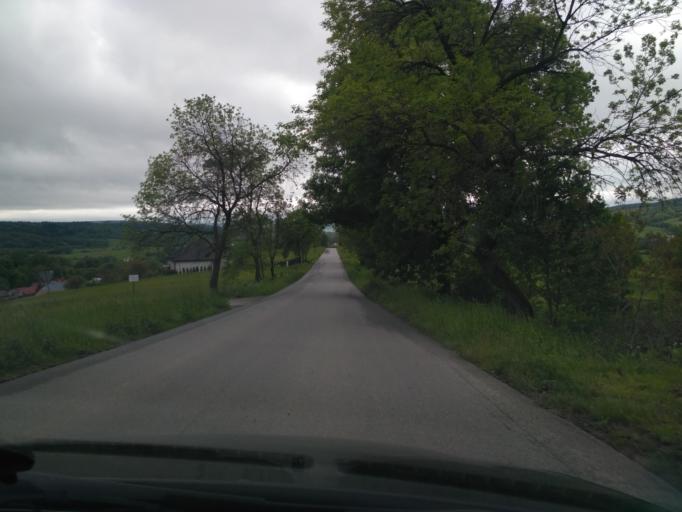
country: PL
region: Subcarpathian Voivodeship
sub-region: Powiat jasielski
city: Jaslo
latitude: 49.8034
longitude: 21.5014
